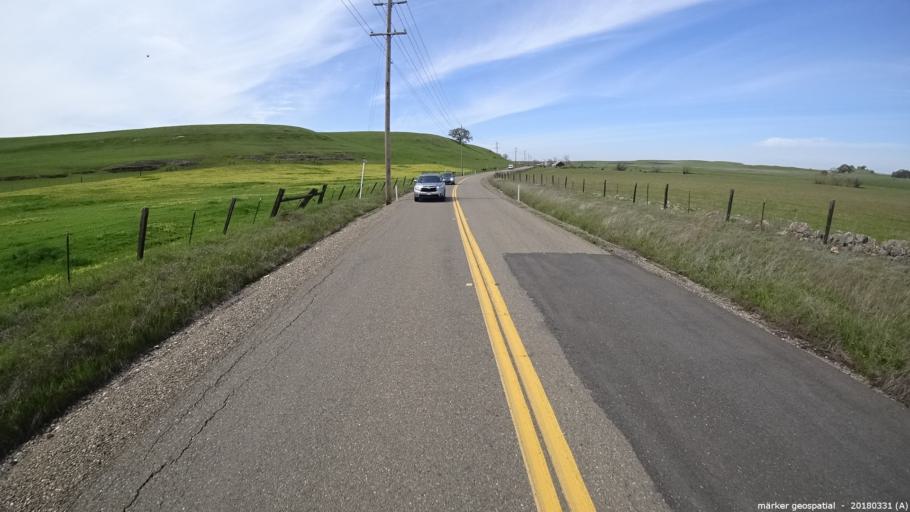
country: US
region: California
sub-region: Sacramento County
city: Rancho Murieta
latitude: 38.5166
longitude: -121.1136
